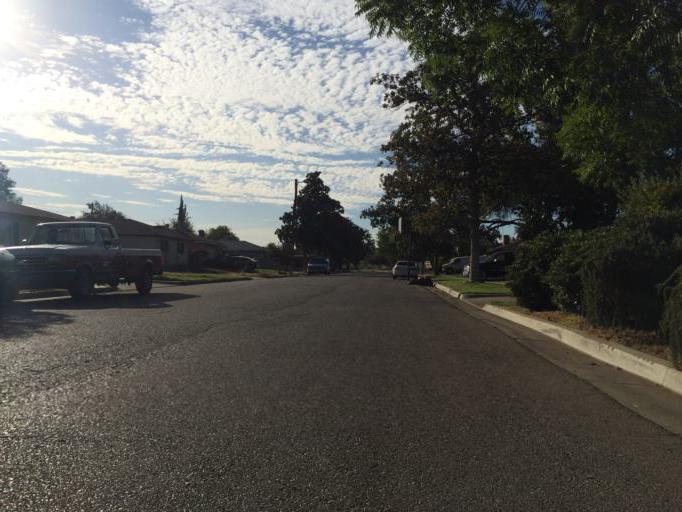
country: US
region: California
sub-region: Fresno County
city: Sunnyside
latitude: 36.7617
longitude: -119.7337
